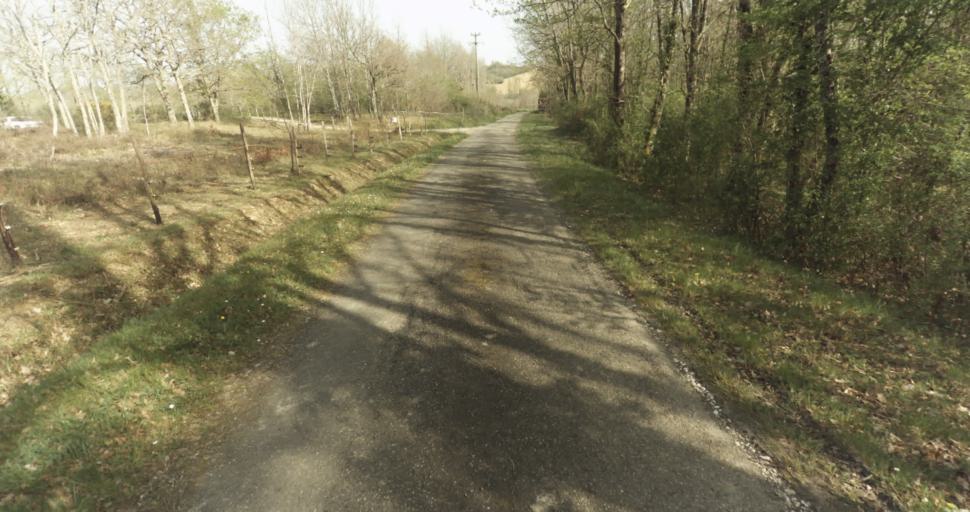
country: FR
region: Midi-Pyrenees
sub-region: Departement du Tarn-et-Garonne
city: Lafrancaise
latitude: 44.1484
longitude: 1.1737
